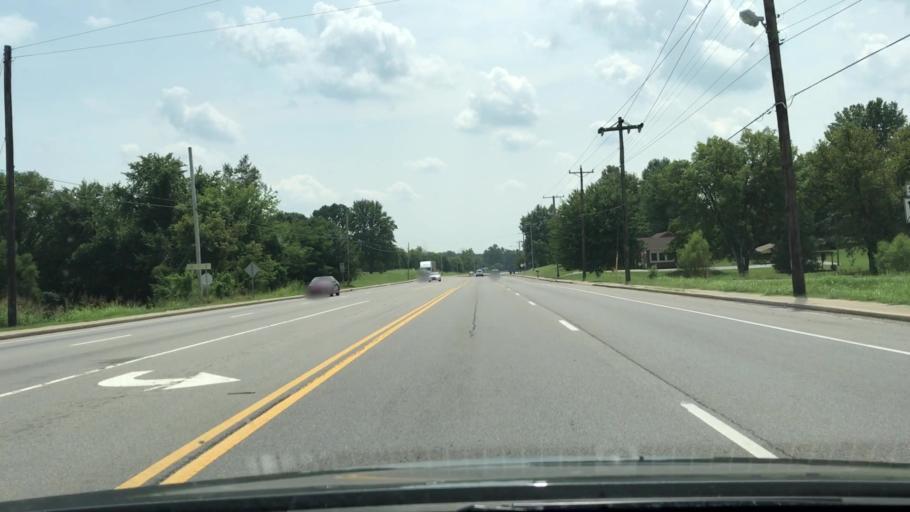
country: US
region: Tennessee
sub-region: Sumner County
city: Portland
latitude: 36.5486
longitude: -86.5063
